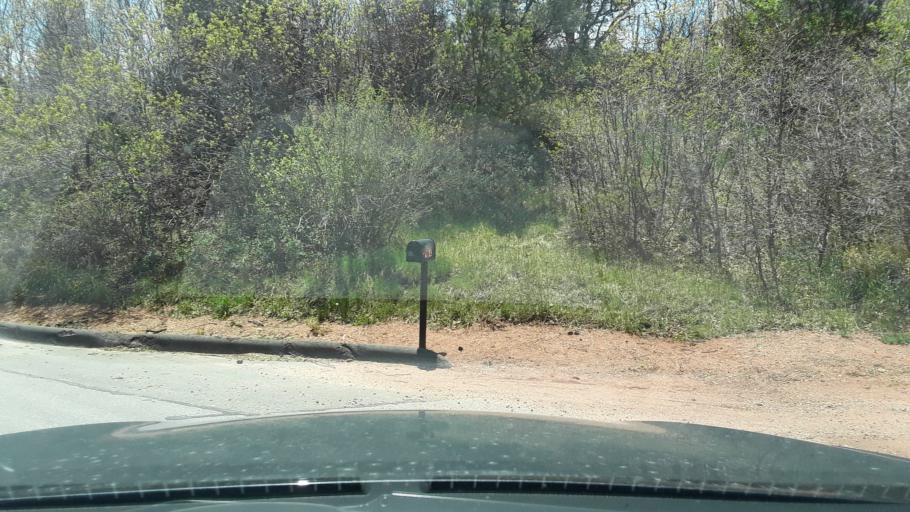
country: US
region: Colorado
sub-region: El Paso County
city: Manitou Springs
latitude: 38.8666
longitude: -104.8851
